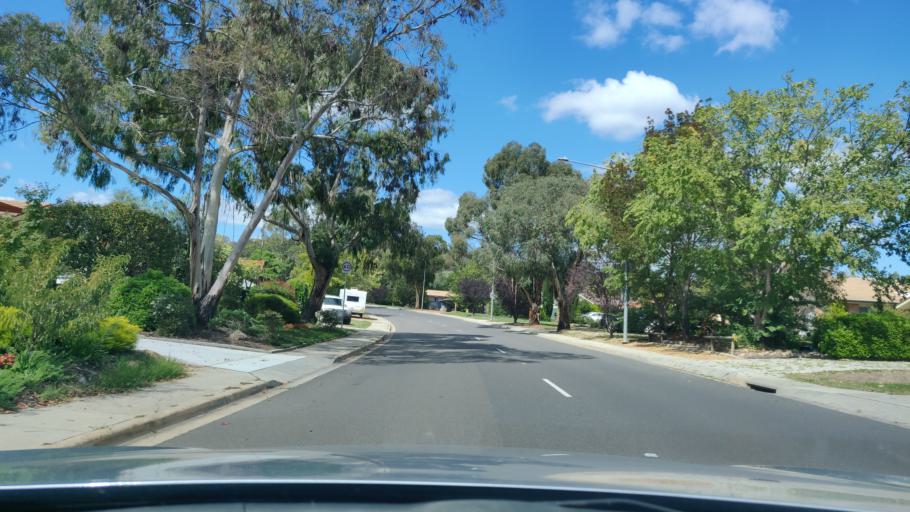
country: AU
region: Australian Capital Territory
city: Macarthur
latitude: -35.4312
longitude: 149.0752
